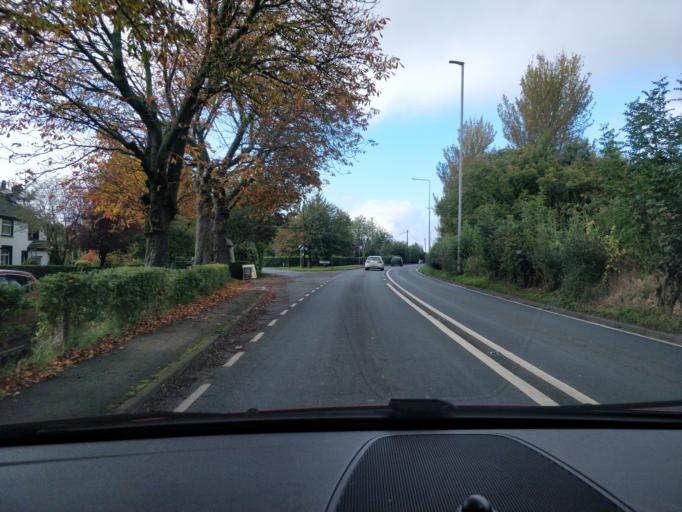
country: GB
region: England
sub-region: Lancashire
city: Ormskirk
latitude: 53.5886
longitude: -2.9154
